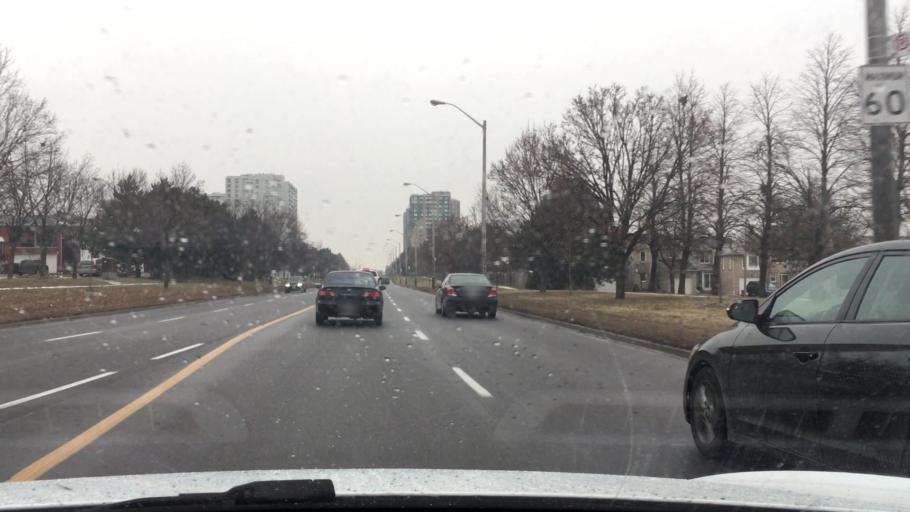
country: CA
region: Ontario
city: Markham
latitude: 43.8185
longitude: -79.2722
